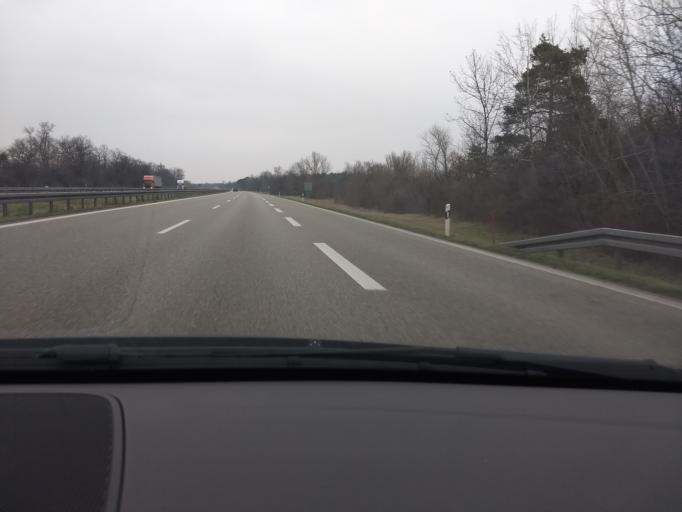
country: DE
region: Baden-Wuerttemberg
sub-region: Freiburg Region
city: Neuenburg am Rhein
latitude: 47.8320
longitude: 7.5641
